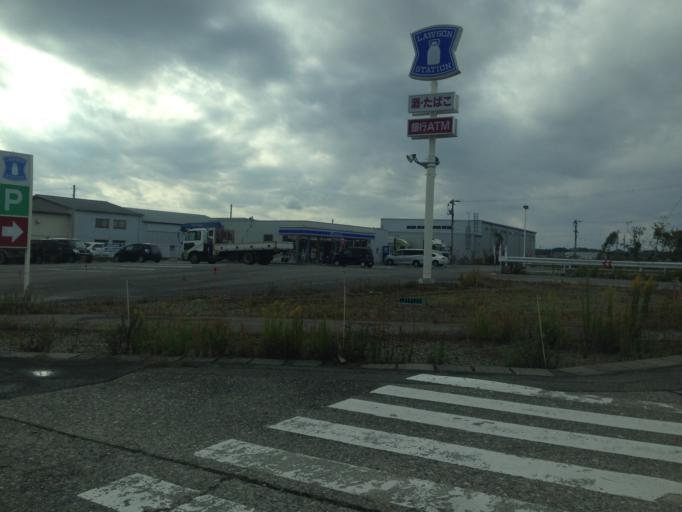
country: JP
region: Ishikawa
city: Komatsu
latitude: 36.3083
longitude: 136.3698
